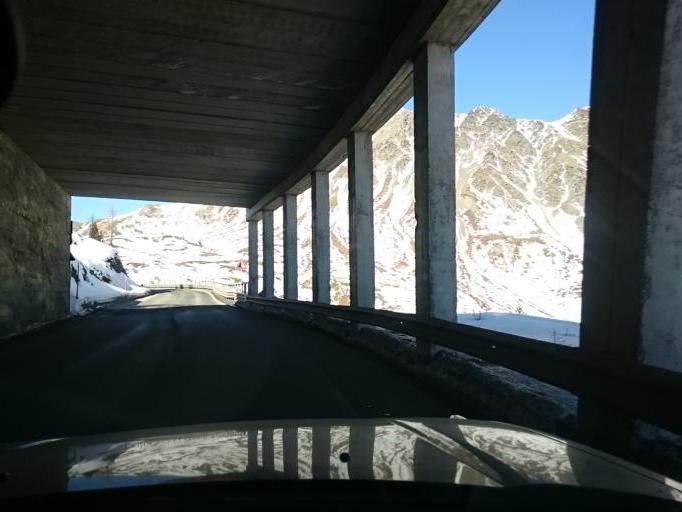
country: IT
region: Lombardy
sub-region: Provincia di Sondrio
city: Isolaccia
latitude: 46.4878
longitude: 10.2208
